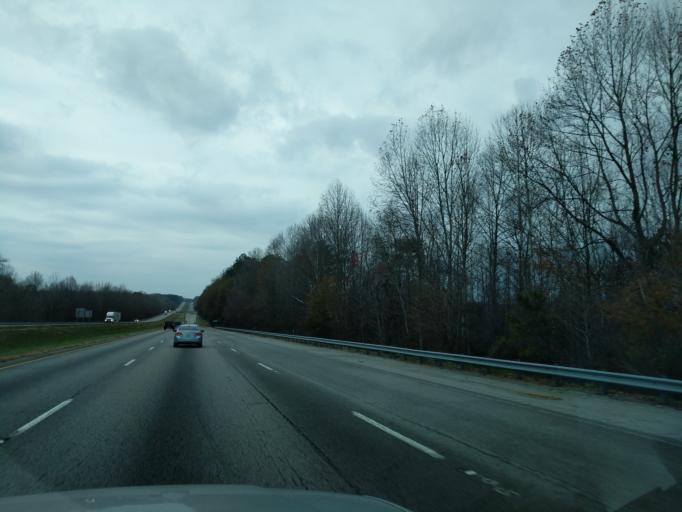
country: US
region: Georgia
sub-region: Franklin County
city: Carnesville
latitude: 34.3742
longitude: -83.2610
